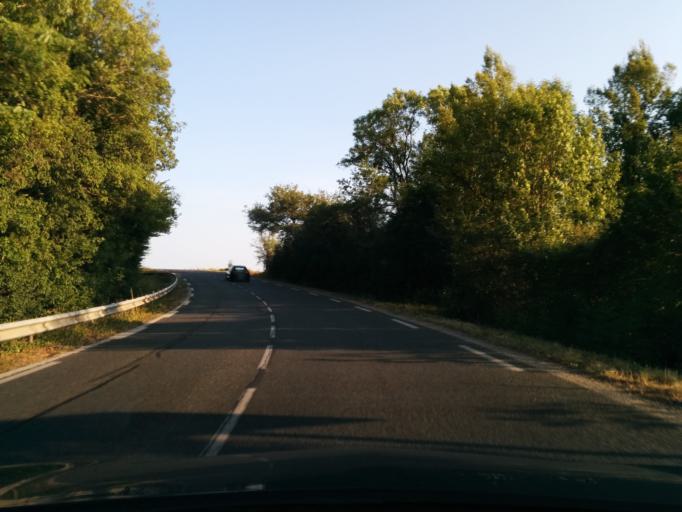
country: FR
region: Midi-Pyrenees
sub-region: Departement du Lot
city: Pradines
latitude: 44.5542
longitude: 1.4768
